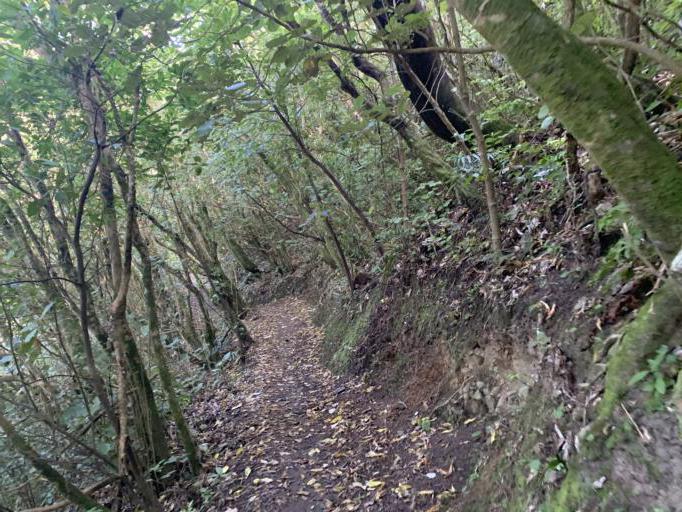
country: NZ
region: Wellington
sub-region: Wellington City
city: Brooklyn
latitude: -41.3001
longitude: 174.7535
